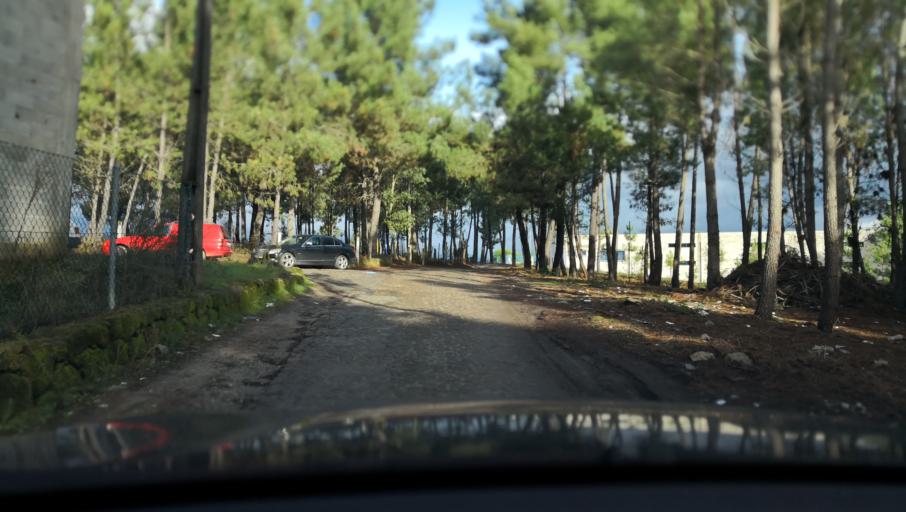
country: PT
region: Vila Real
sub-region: Vila Real
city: Vila Real
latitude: 41.2737
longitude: -7.7159
